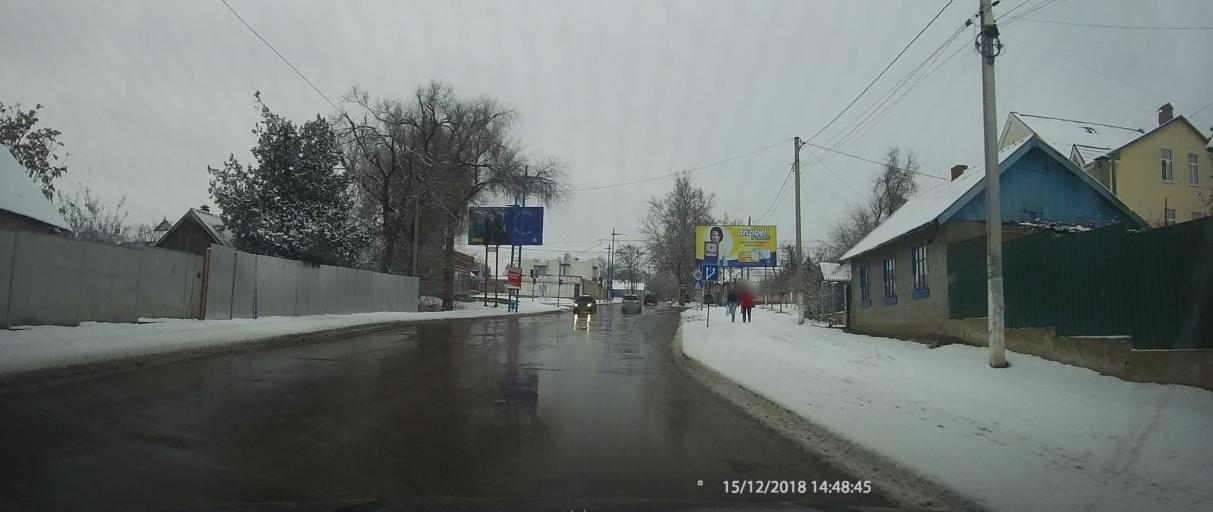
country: MD
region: Cahul
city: Cahul
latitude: 45.8997
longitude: 28.1964
